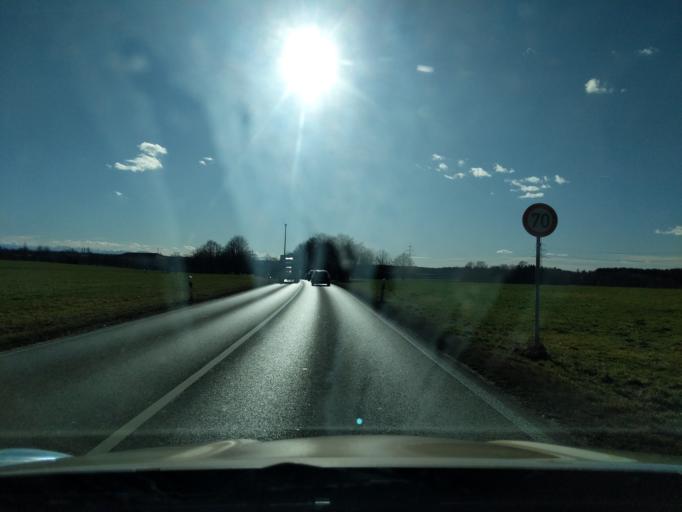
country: DE
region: Bavaria
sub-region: Upper Bavaria
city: Zorneding
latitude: 48.0979
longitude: 11.8253
